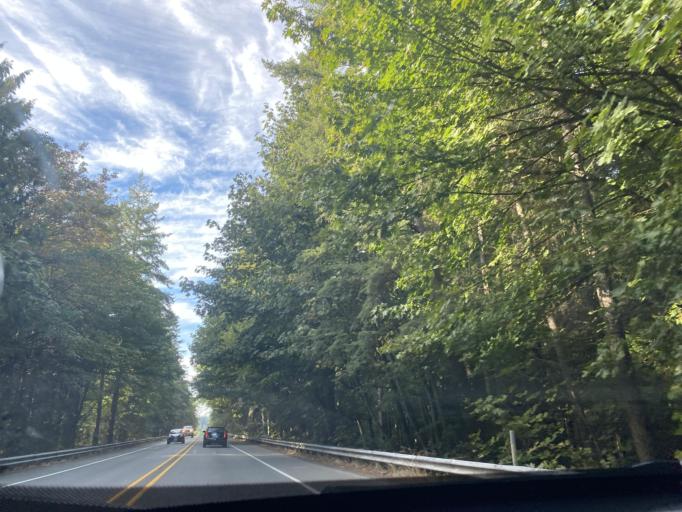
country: US
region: Washington
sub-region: Kitsap County
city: Suquamish
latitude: 47.6828
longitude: -122.5428
